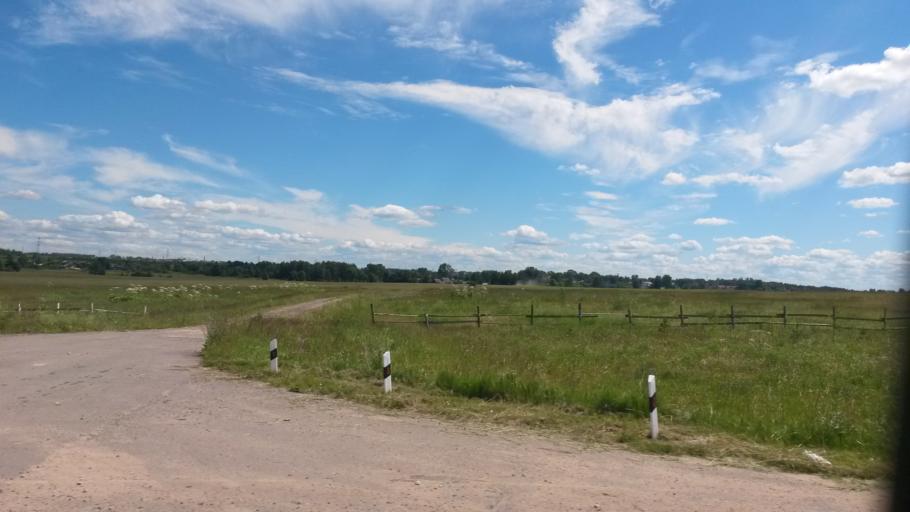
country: RU
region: Ivanovo
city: Staraya Vichuga
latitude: 57.2327
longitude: 41.8722
